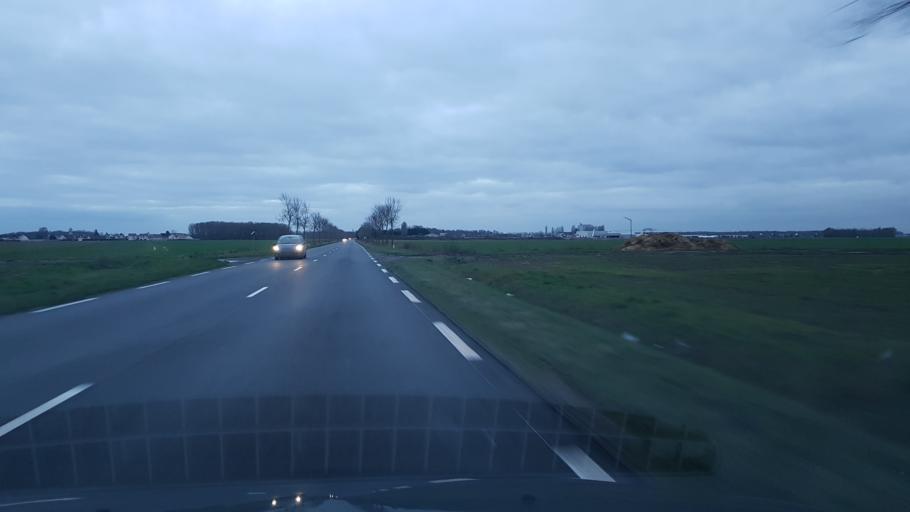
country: FR
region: Ile-de-France
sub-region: Departement de Seine-et-Marne
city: Soignolles-en-Brie
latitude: 48.6313
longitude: 2.6809
